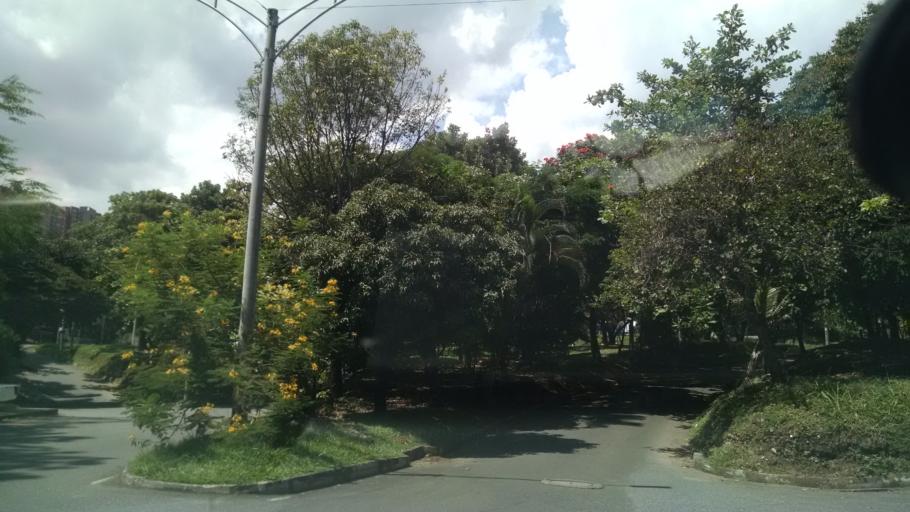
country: CO
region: Antioquia
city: Itagui
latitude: 6.2224
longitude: -75.5988
